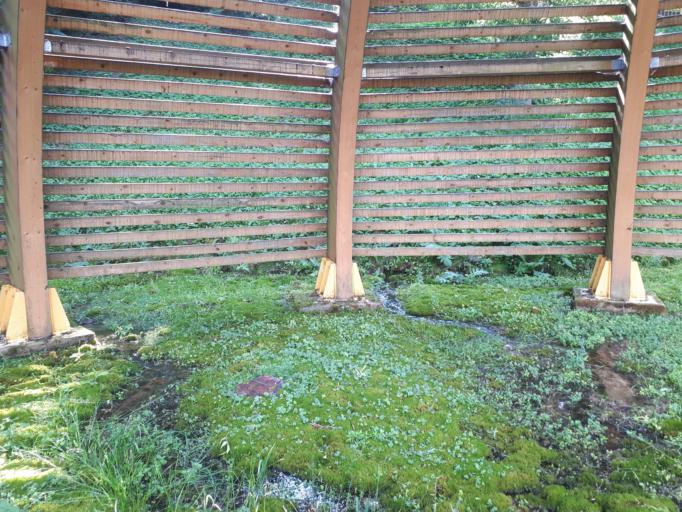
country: LT
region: Utenos apskritis
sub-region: Anyksciai
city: Anyksciai
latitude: 55.4315
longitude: 24.9286
